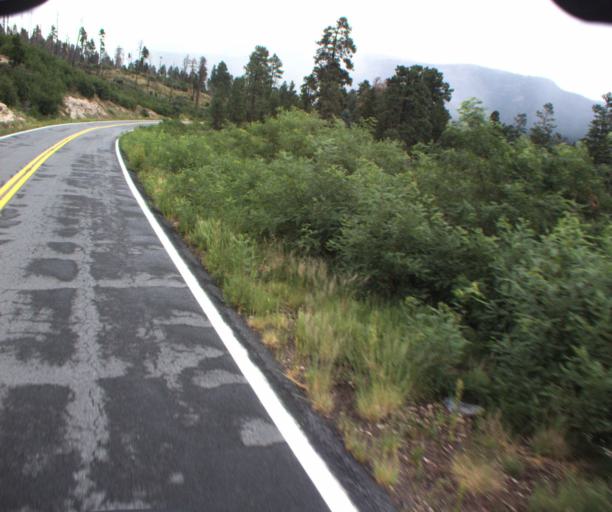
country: US
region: Arizona
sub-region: Apache County
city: Eagar
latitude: 33.8213
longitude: -109.1549
